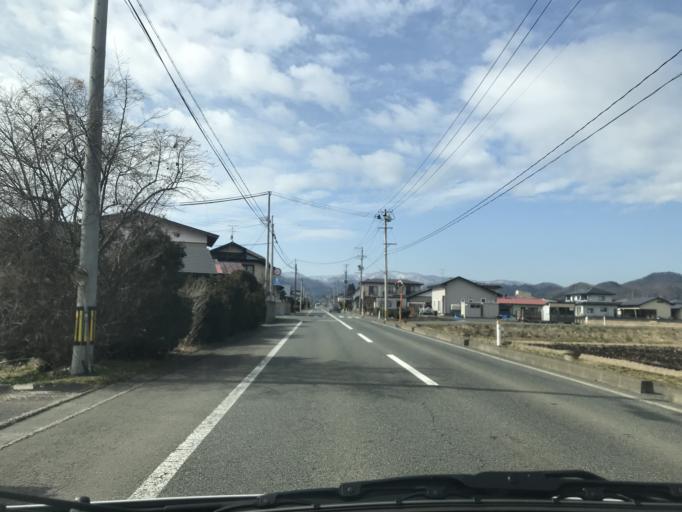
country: JP
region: Iwate
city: Hanamaki
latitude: 39.3872
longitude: 141.0608
